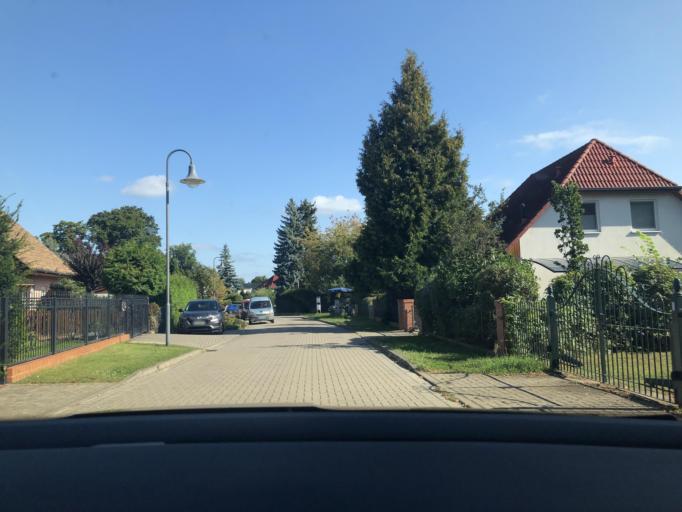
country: DE
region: Brandenburg
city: Erkner
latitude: 52.4145
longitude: 13.7376
